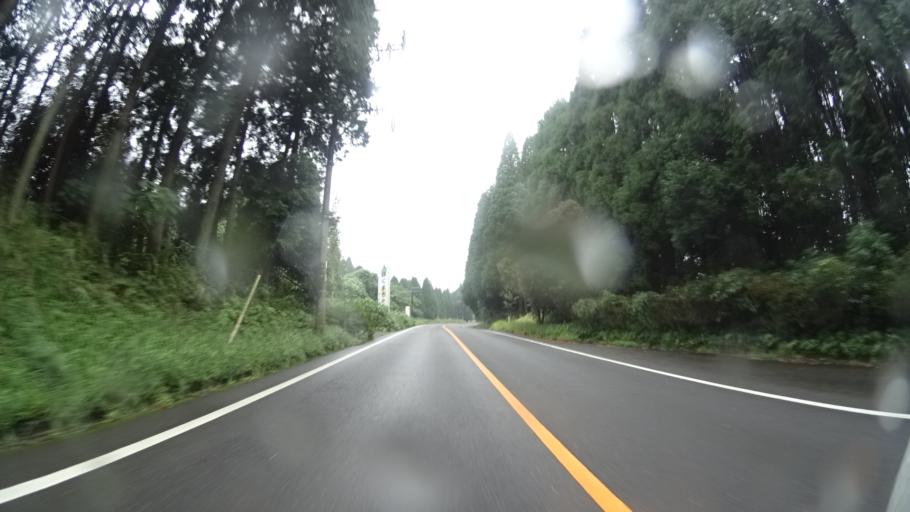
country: JP
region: Kagoshima
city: Kajiki
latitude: 31.8010
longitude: 130.6716
